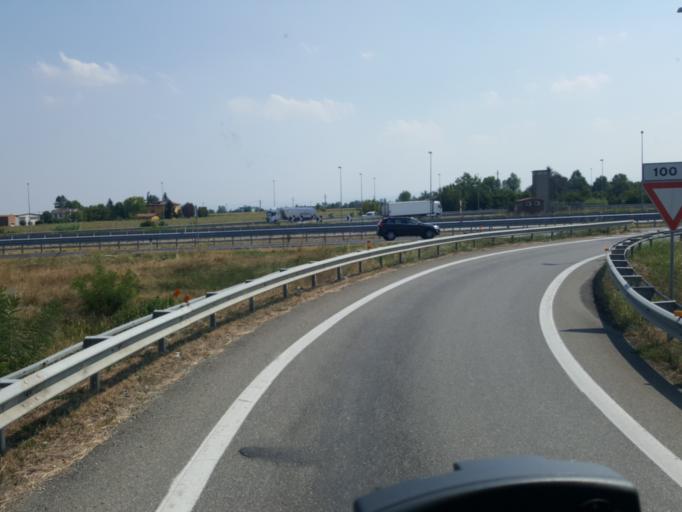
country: IT
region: Emilia-Romagna
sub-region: Provincia di Piacenza
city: Caorso
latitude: 45.0577
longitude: 9.8904
